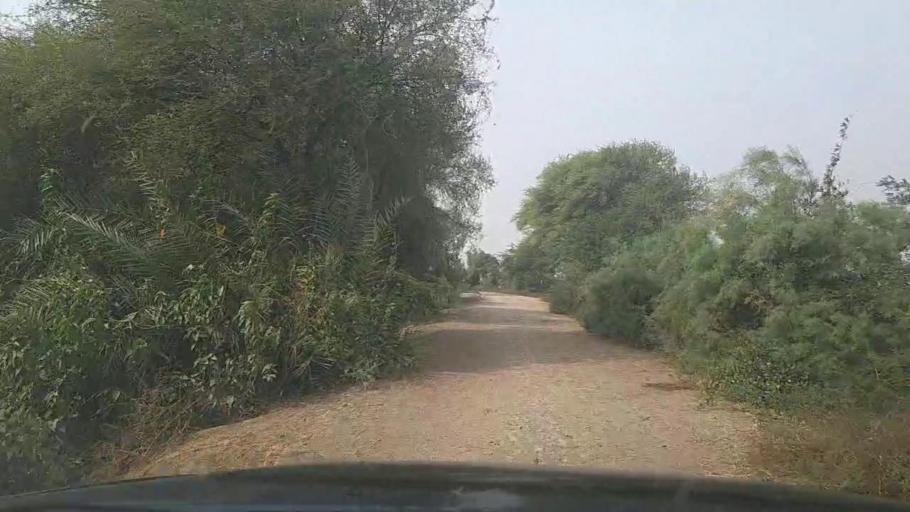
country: PK
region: Sindh
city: Mirpur Sakro
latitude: 24.5294
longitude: 67.7960
